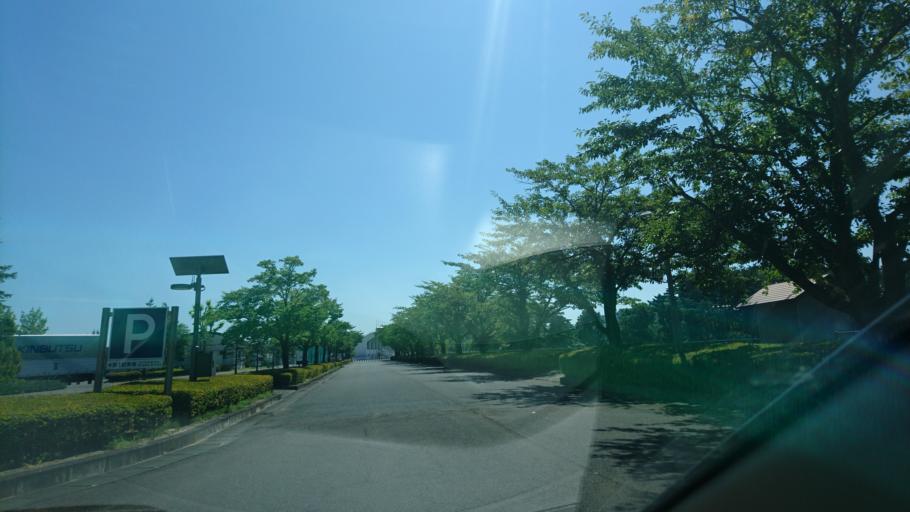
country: JP
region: Iwate
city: Kitakami
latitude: 39.2613
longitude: 141.0949
